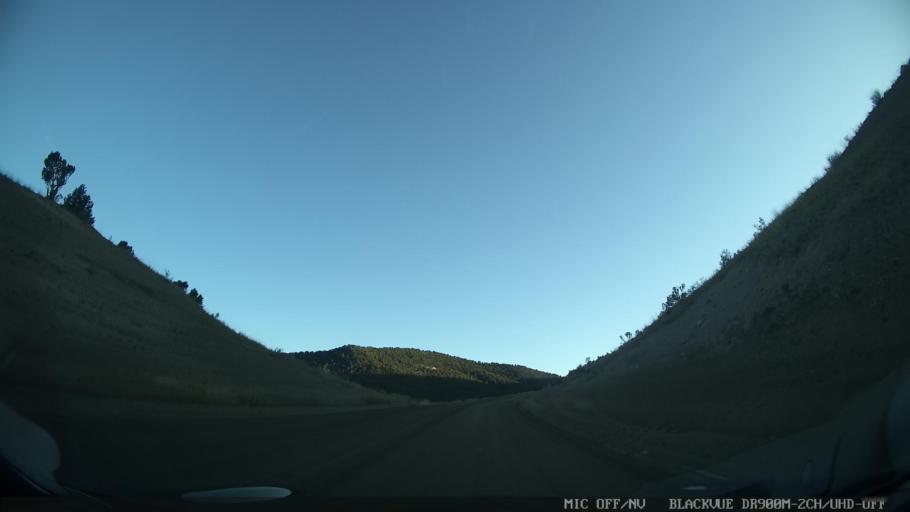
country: US
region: Colorado
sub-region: Grand County
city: Kremmling
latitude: 39.9462
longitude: -106.5289
